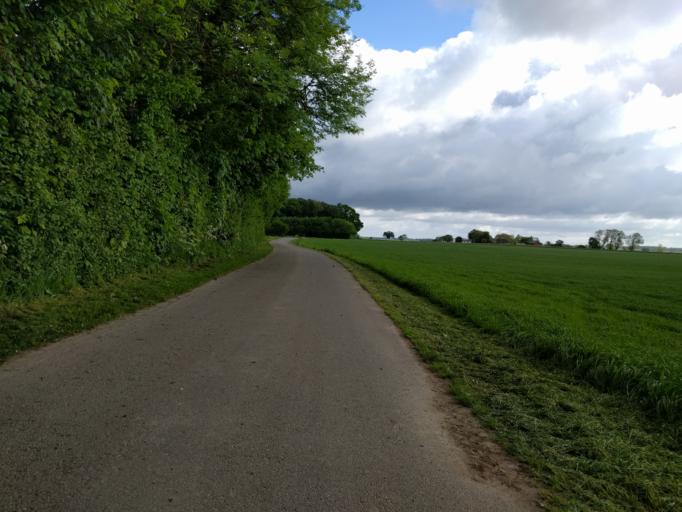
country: DK
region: South Denmark
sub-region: Kerteminde Kommune
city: Kerteminde
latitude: 55.4183
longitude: 10.6261
